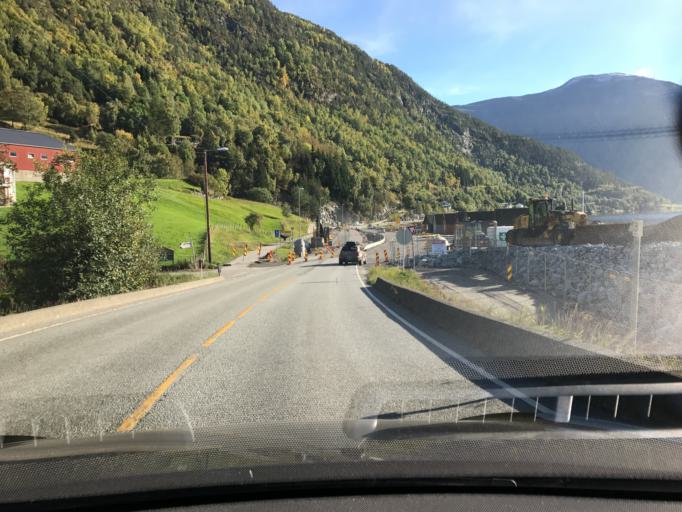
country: NO
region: Sogn og Fjordane
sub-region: Sogndal
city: Sogndalsfjora
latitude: 61.2307
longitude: 7.1232
